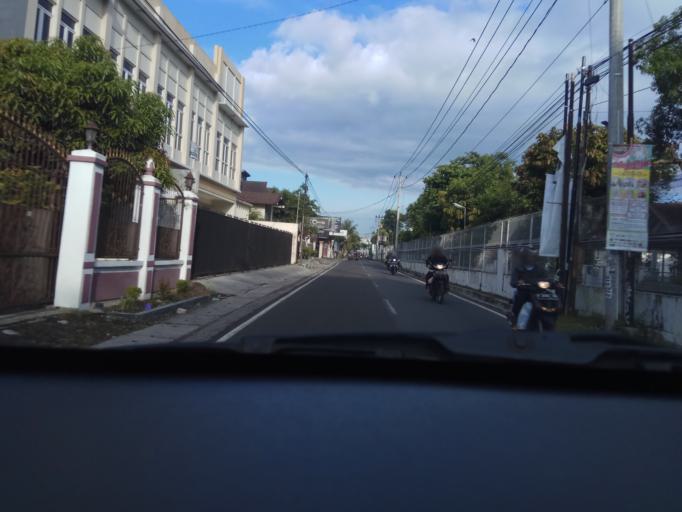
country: ID
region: Daerah Istimewa Yogyakarta
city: Depok
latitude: -7.7639
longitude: 110.4093
